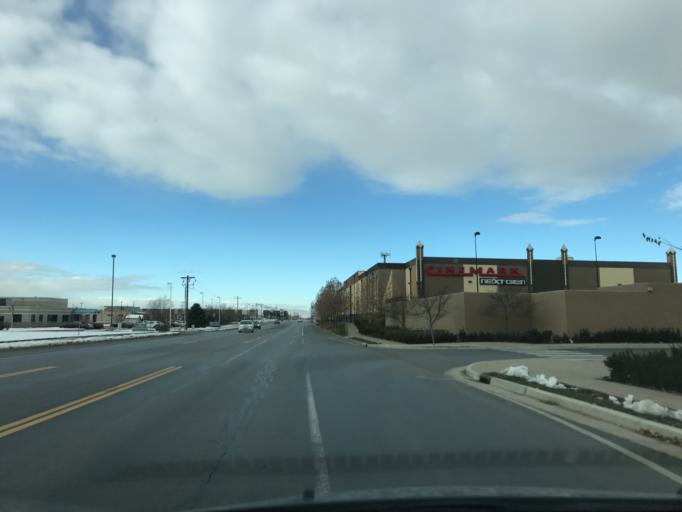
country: US
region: Utah
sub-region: Davis County
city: Farmington
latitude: 40.9821
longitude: -111.9053
